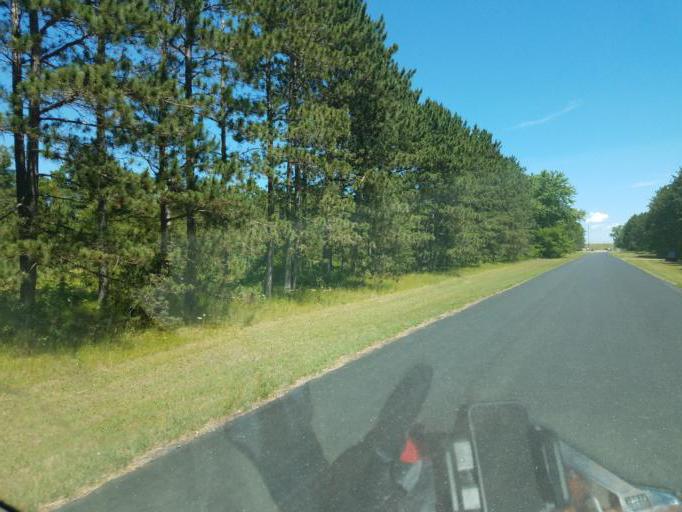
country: US
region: Wisconsin
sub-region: Juneau County
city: New Lisbon
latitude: 44.0537
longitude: -90.0274
